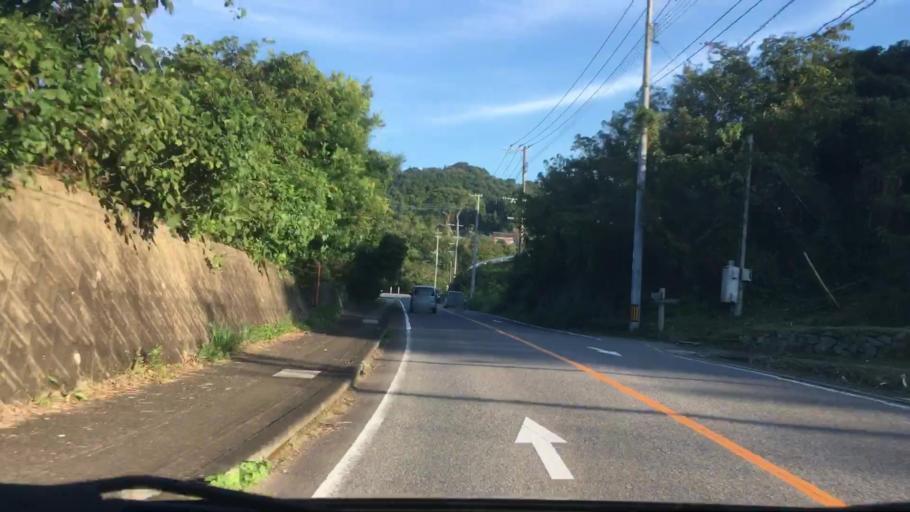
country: JP
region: Nagasaki
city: Sasebo
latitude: 33.0459
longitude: 129.7265
